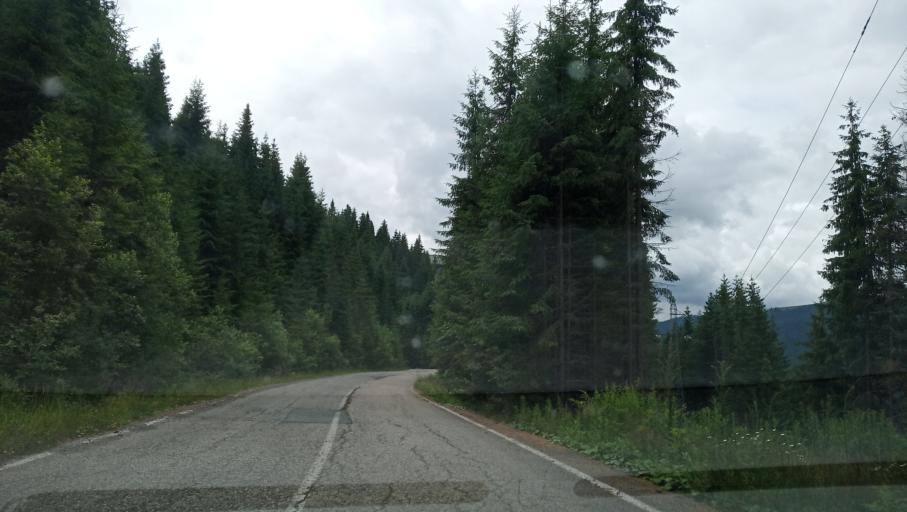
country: RO
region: Valcea
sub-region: Comuna Voineasa
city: Voineasa
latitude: 45.4276
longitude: 23.7389
